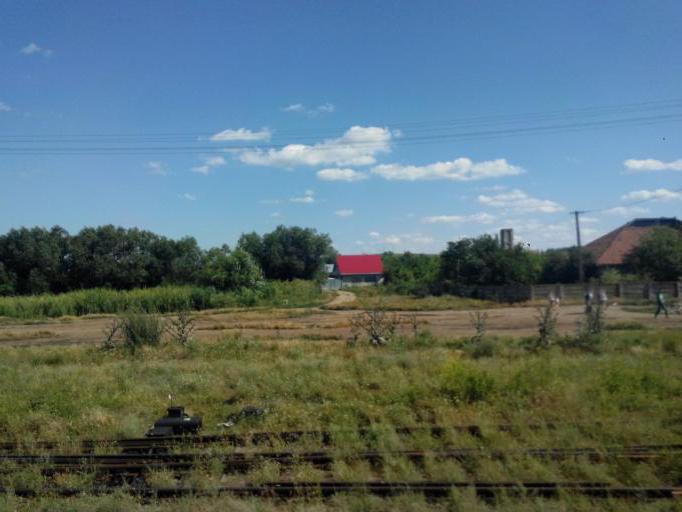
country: RO
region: Vaslui
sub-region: Municipiul Barlad
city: Barlad
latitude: 46.2114
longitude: 27.6647
